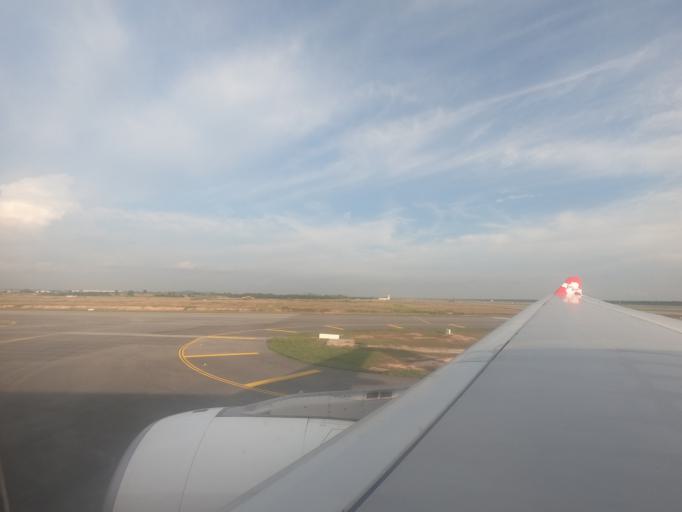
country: MY
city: Sungai Pelek New Village
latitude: 2.7350
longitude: 101.6852
